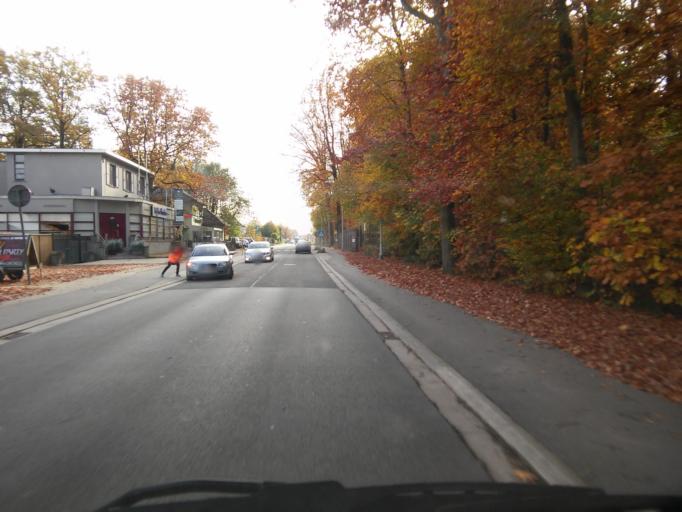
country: BE
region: Flanders
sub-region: Provincie Oost-Vlaanderen
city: Buggenhout
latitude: 50.9984
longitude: 4.2105
